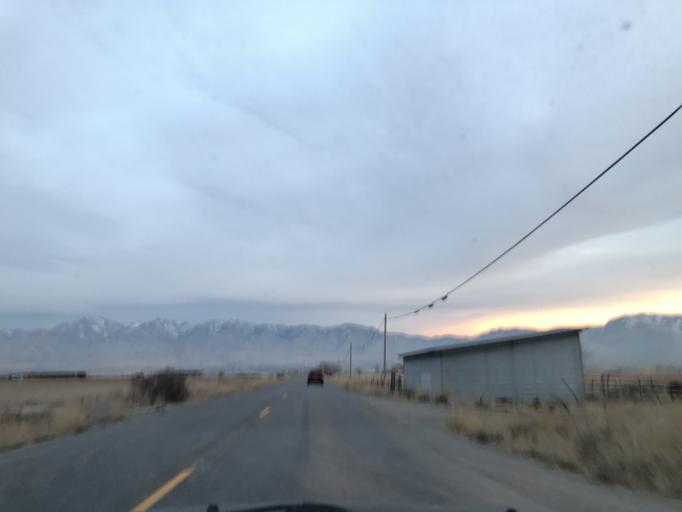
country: US
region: Utah
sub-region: Cache County
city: Benson
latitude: 41.7948
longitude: -111.8999
